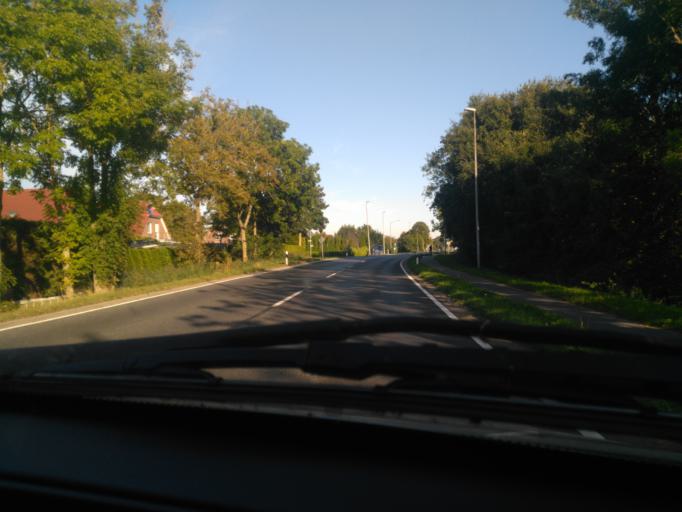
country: DE
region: Lower Saxony
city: Emden
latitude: 53.3367
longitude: 7.2596
